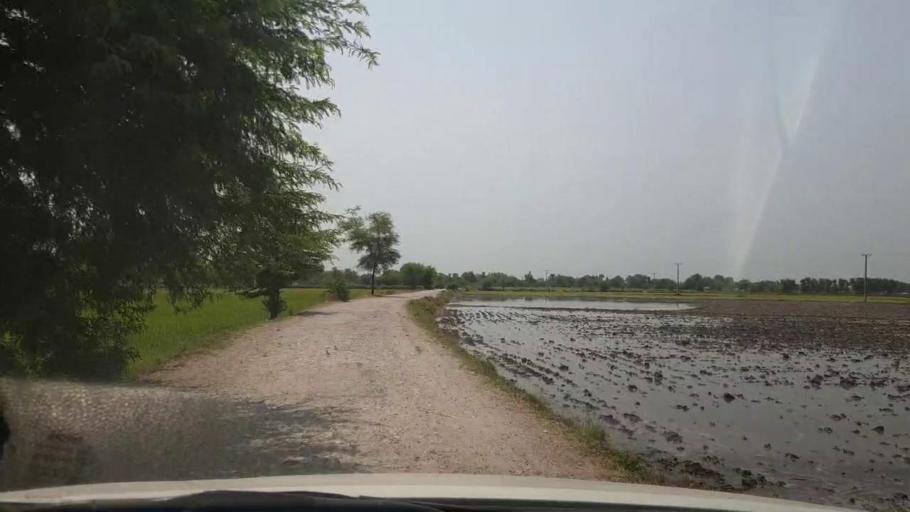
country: PK
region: Sindh
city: Rustam jo Goth
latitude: 27.9831
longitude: 68.7203
